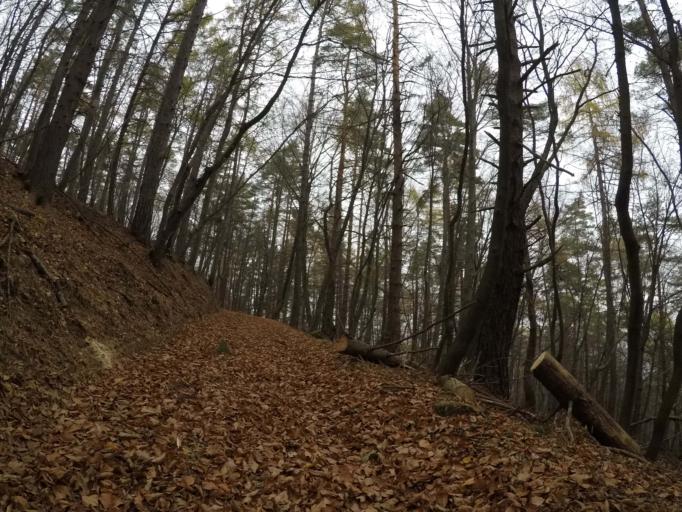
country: SK
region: Presovsky
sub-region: Okres Presov
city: Presov
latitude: 48.9028
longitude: 21.1690
